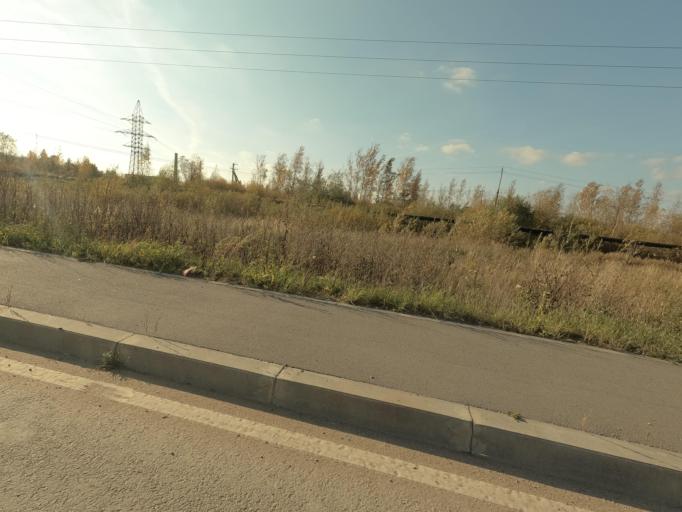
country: RU
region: Leningrad
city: Mga
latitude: 59.7505
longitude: 31.0882
